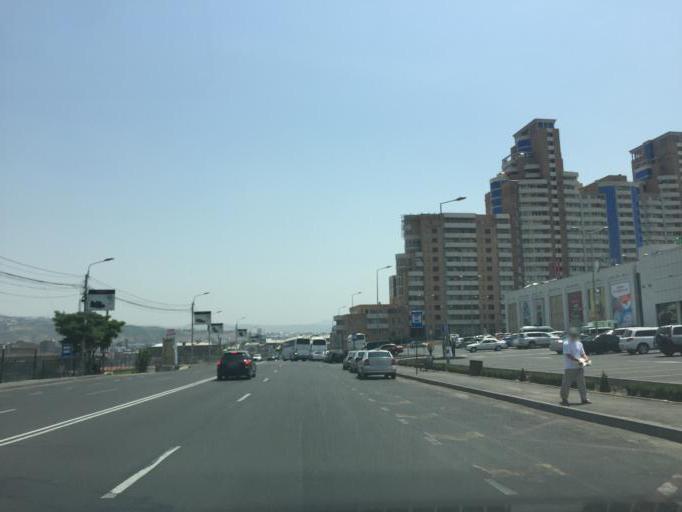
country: AM
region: Yerevan
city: Yerevan
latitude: 40.1807
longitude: 44.4880
